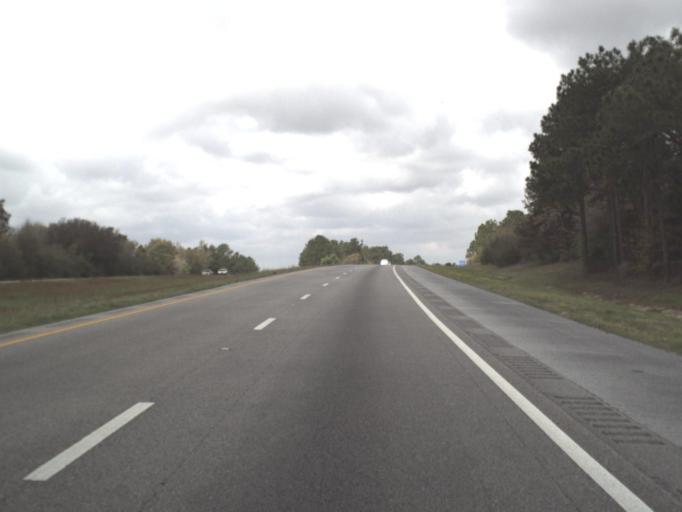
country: US
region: Florida
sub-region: Okaloosa County
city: Crestview
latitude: 30.7200
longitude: -86.4696
